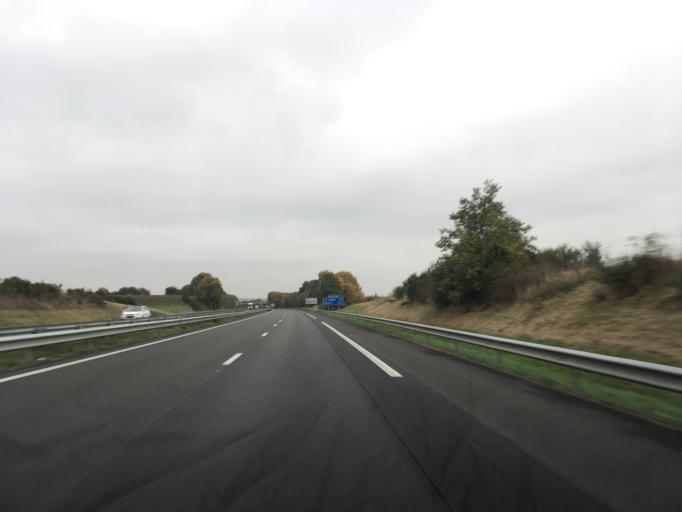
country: FR
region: Pays de la Loire
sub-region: Departement de Maine-et-Loire
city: Durtal
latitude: 47.6750
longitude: -0.2566
